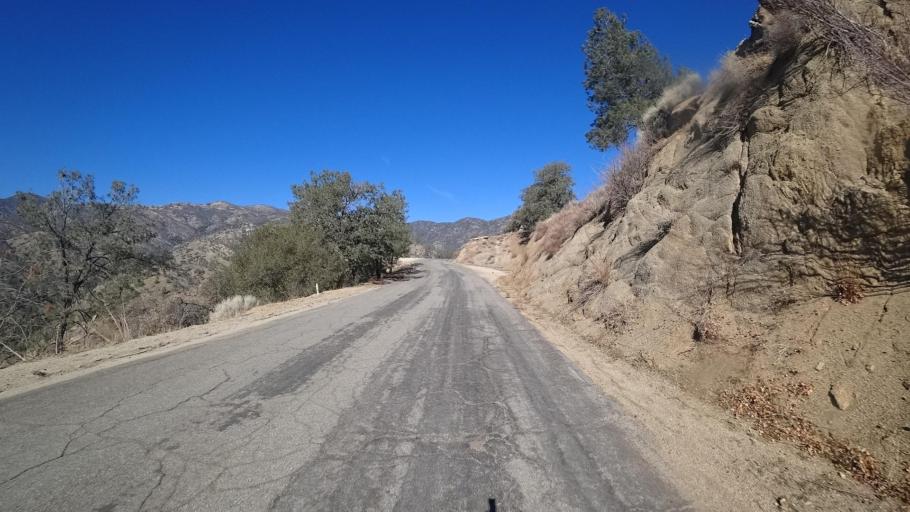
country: US
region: California
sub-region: Kern County
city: Bodfish
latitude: 35.5497
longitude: -118.6113
